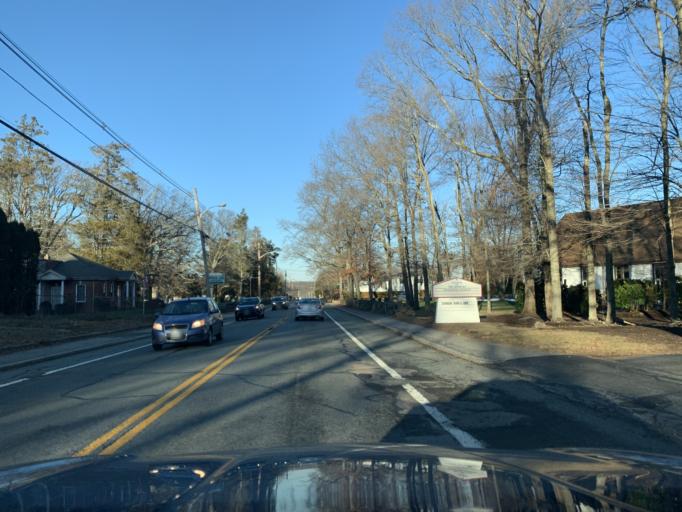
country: US
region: Rhode Island
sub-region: Kent County
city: West Warwick
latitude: 41.7128
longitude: -71.5359
